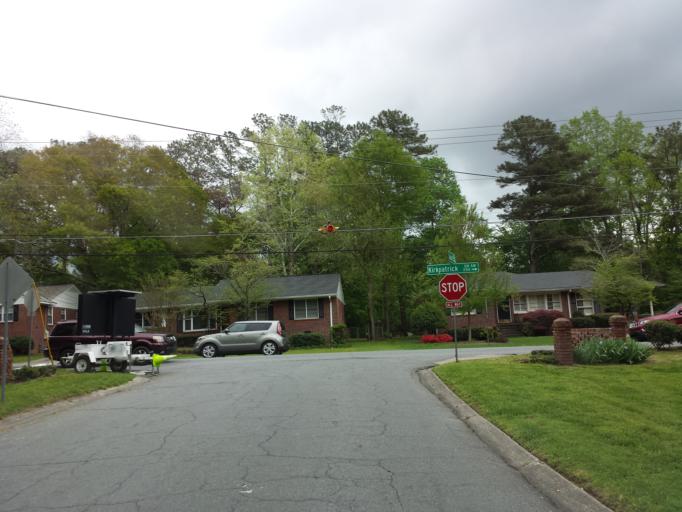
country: US
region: Georgia
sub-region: Cobb County
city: Marietta
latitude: 33.9466
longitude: -84.5694
